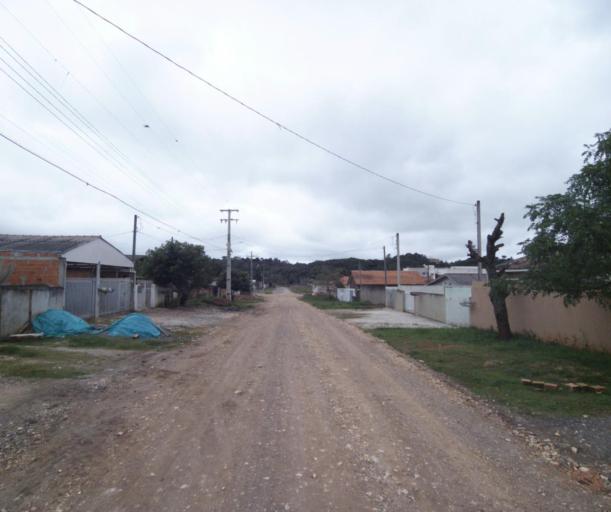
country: BR
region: Parana
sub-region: Quatro Barras
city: Quatro Barras
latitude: -25.3594
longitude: -49.0948
